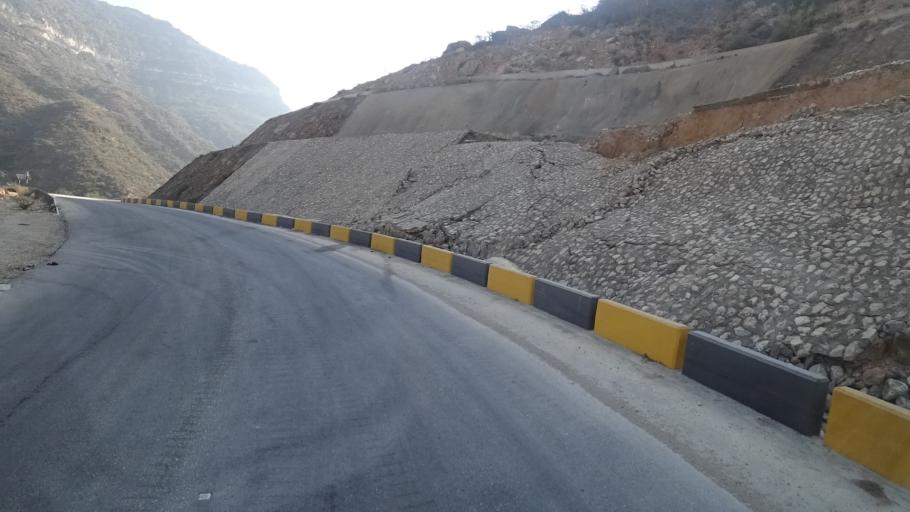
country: YE
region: Al Mahrah
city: Hawf
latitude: 16.7481
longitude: 53.2245
